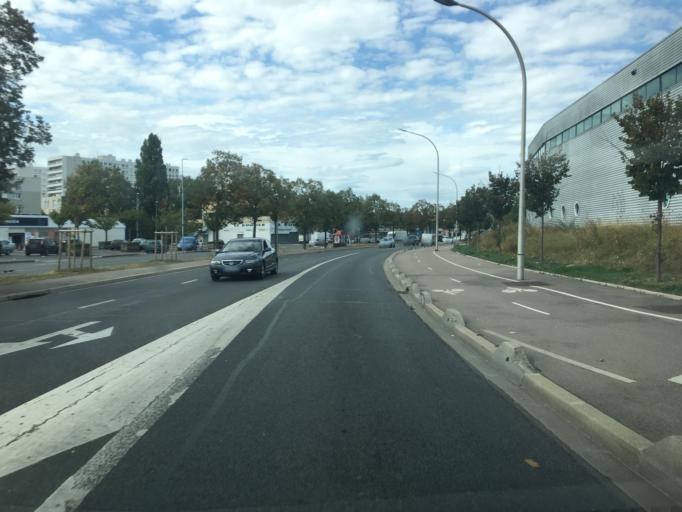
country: FR
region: Ile-de-France
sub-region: Departement du Val-de-Marne
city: Valenton
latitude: 48.7494
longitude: 2.4552
